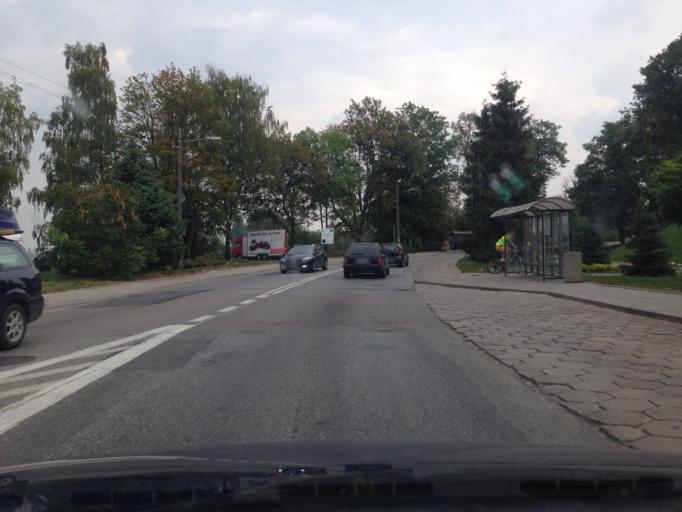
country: PL
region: Pomeranian Voivodeship
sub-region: Powiat sztumski
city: Sztum
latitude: 53.9158
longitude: 19.0395
